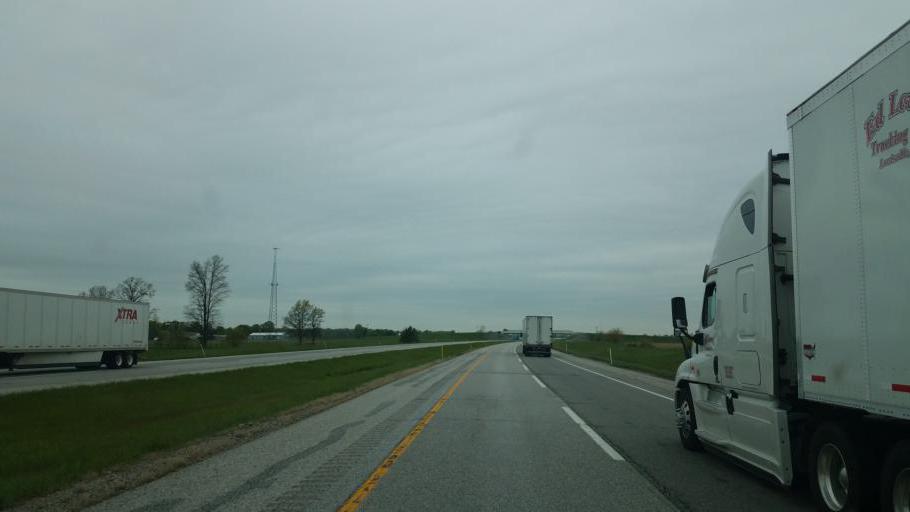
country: US
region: Michigan
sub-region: Saint Joseph County
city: Sturgis
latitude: 41.7463
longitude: -85.5076
